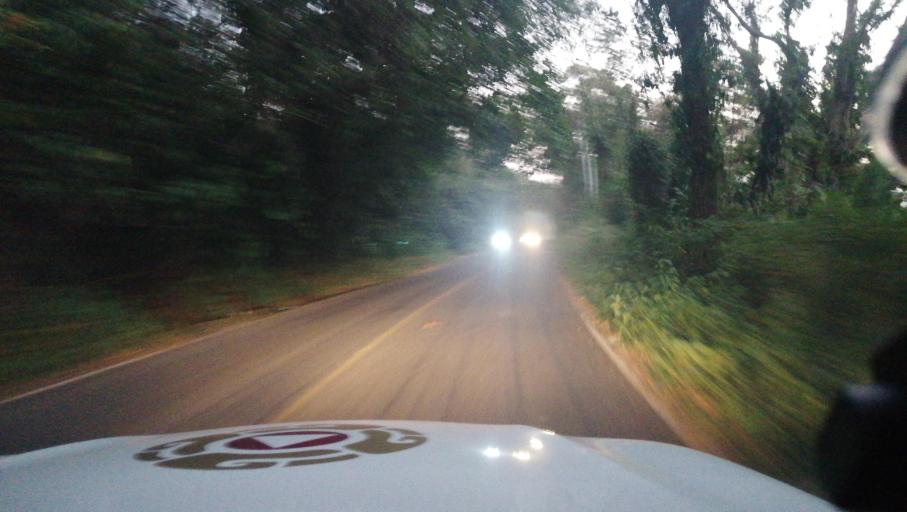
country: MX
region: Chiapas
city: Veinte de Noviembre
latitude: 14.9882
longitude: -92.2417
